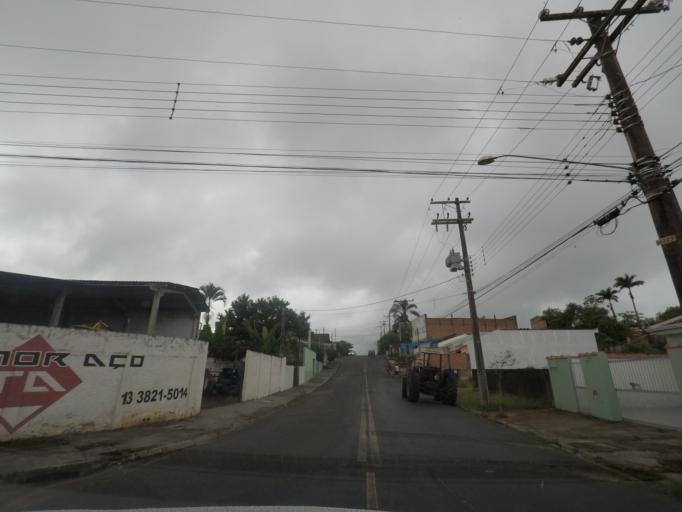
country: BR
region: Sao Paulo
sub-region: Registro
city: Registro
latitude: -24.5077
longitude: -47.8539
